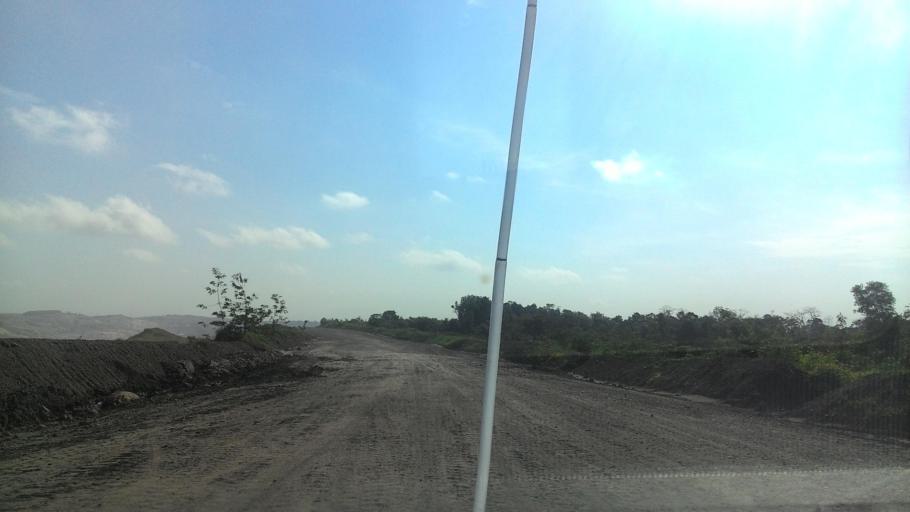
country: ID
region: South Kalimantan
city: Tanta
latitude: -2.1873
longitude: 115.4823
